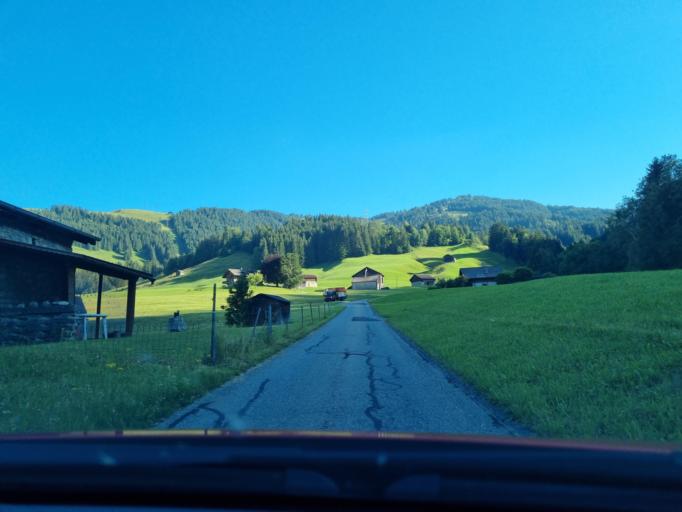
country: CH
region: Vaud
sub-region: Riviera-Pays-d'Enhaut District
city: Chateau-d'Oex
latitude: 46.4610
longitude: 7.1010
